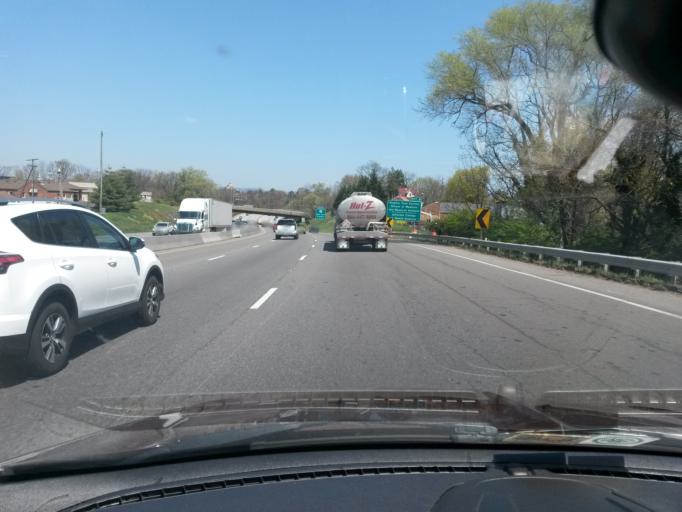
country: US
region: Virginia
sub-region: City of Roanoke
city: Roanoke
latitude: 37.2538
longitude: -79.9550
